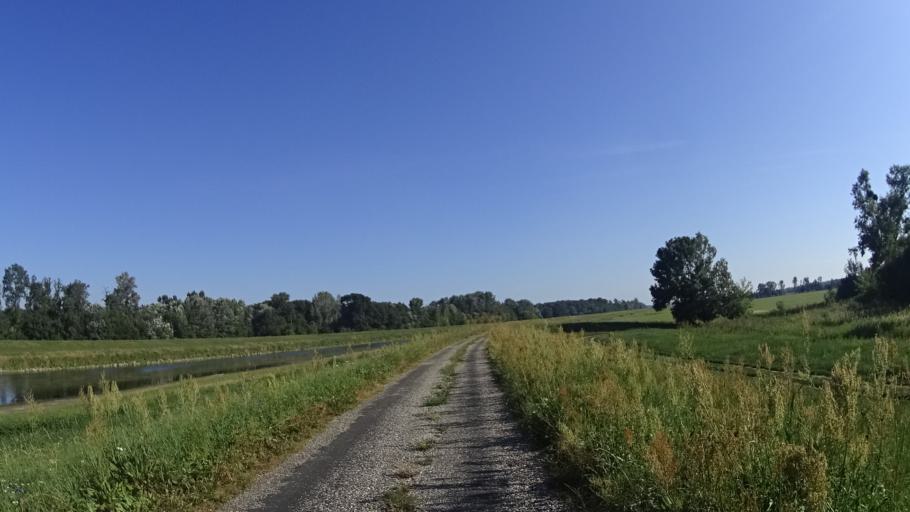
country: CZ
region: South Moravian
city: Tvrdonice
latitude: 48.7274
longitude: 17.0145
